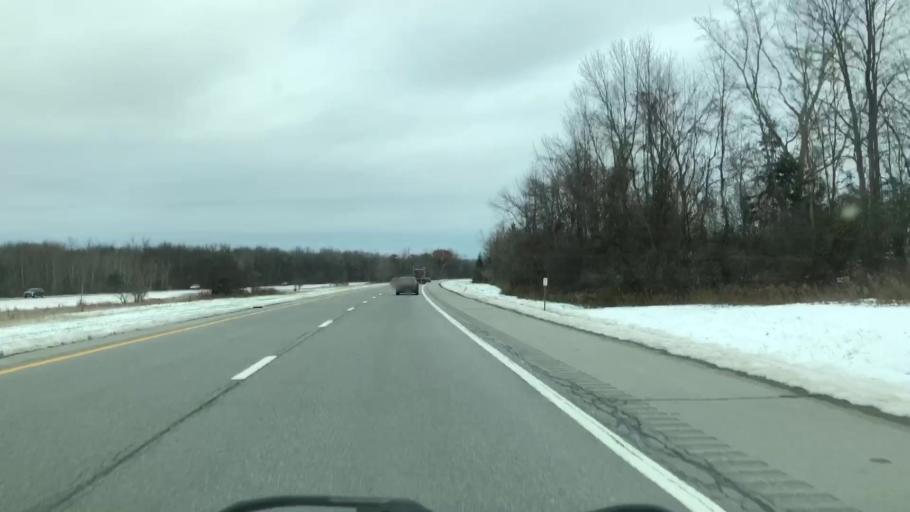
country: US
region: New York
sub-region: Monroe County
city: Spencerport
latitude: 43.1126
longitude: -77.7741
